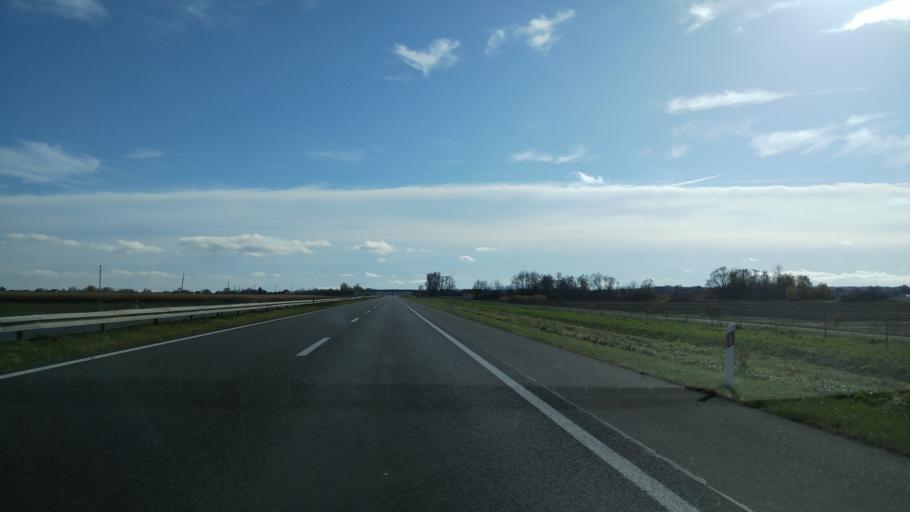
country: HR
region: Sisacko-Moslavacka
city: Lipovljani
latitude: 45.3961
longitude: 16.8636
